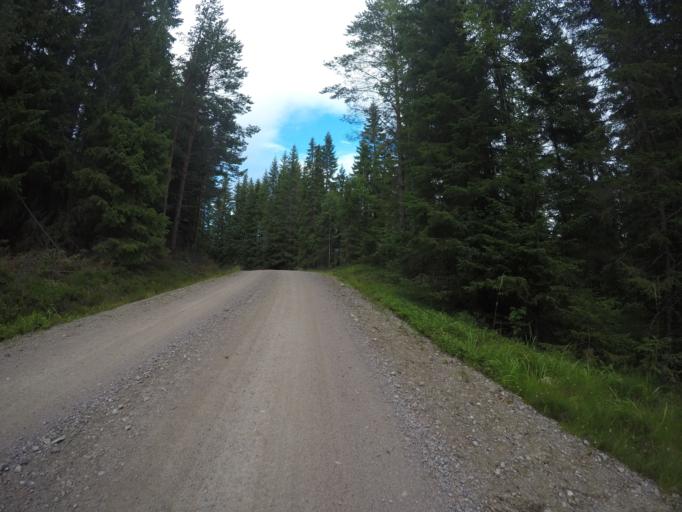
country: SE
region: OErebro
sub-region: Hallefors Kommun
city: Haellefors
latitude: 60.0136
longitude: 14.4381
